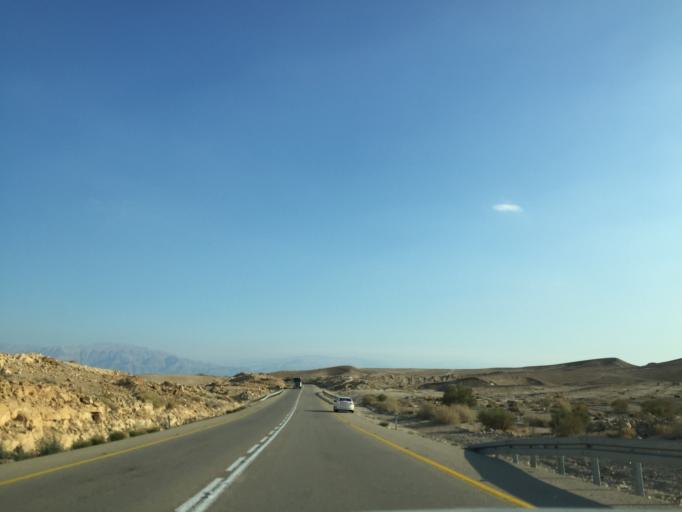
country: IL
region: Southern District
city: `En Boqeq
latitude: 31.1652
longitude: 35.3209
